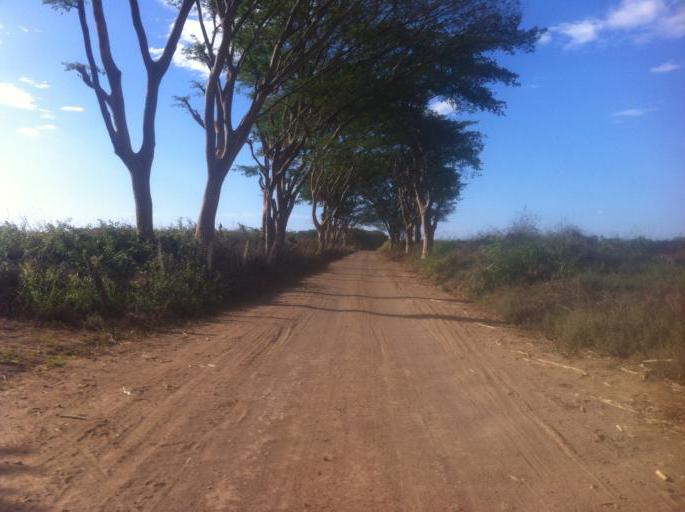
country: NI
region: Managua
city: Masachapa
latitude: 11.8387
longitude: -86.5210
